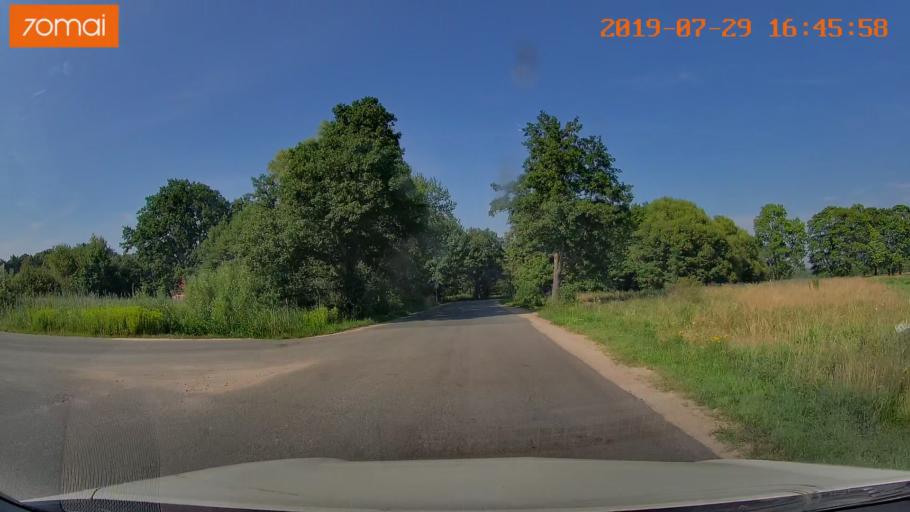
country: RU
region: Kaliningrad
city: Primorsk
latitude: 54.7698
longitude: 20.0800
